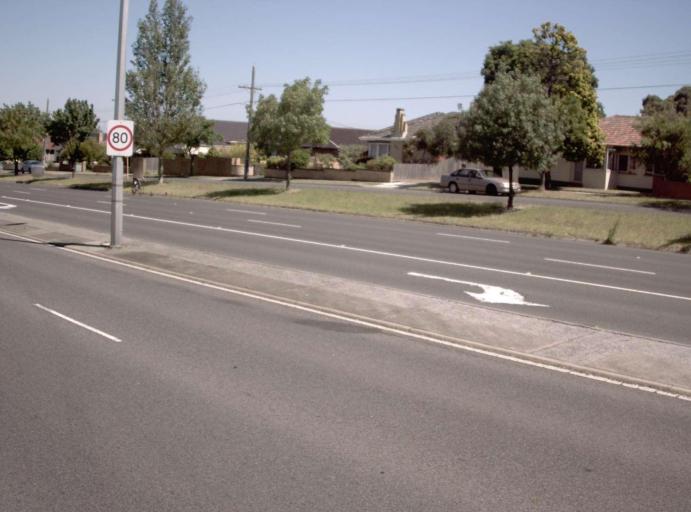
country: AU
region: Victoria
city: Clayton
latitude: -37.9050
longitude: 145.1124
